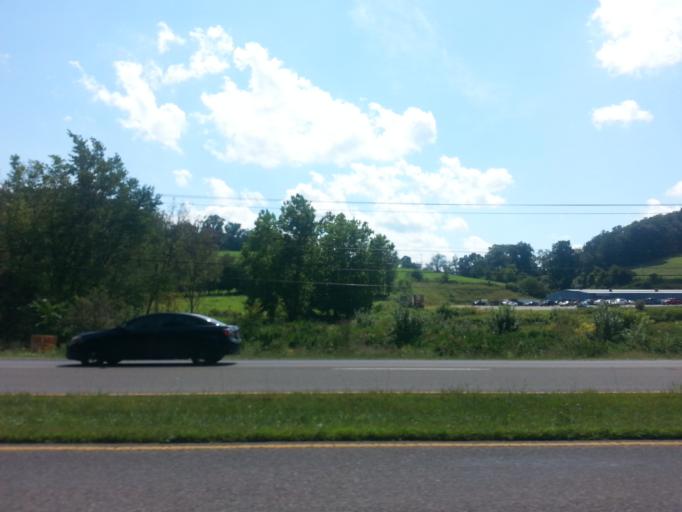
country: US
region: Virginia
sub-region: Washington County
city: Abingdon
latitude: 36.7178
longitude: -82.0070
